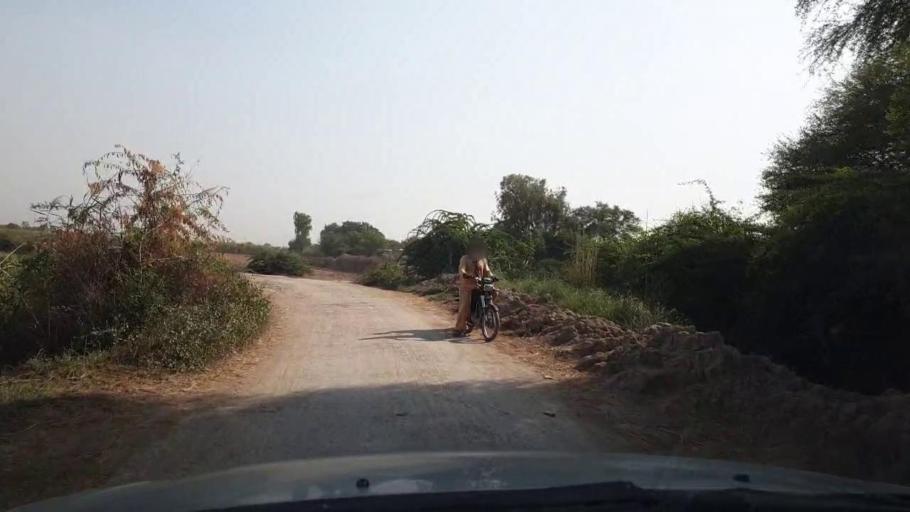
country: PK
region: Sindh
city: Bulri
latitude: 24.9184
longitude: 68.3559
